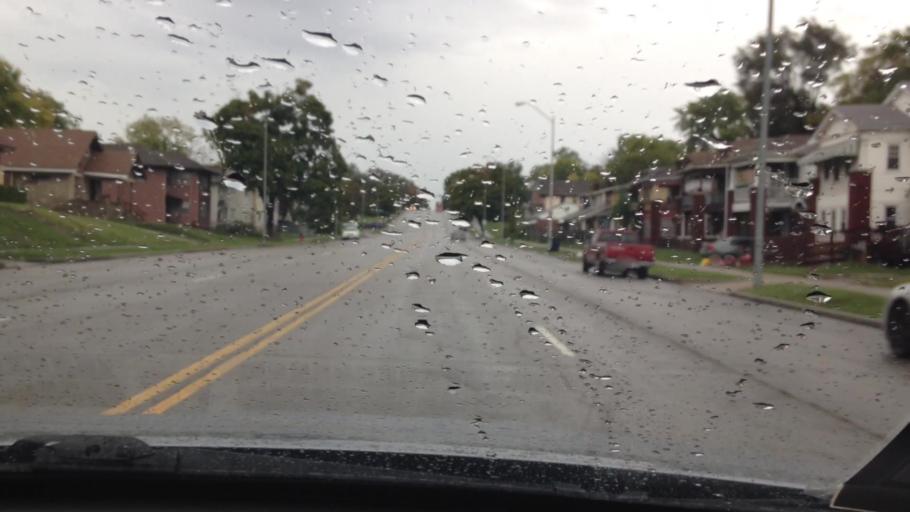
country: US
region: Missouri
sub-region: Jackson County
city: Kansas City
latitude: 39.0524
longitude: -94.5677
